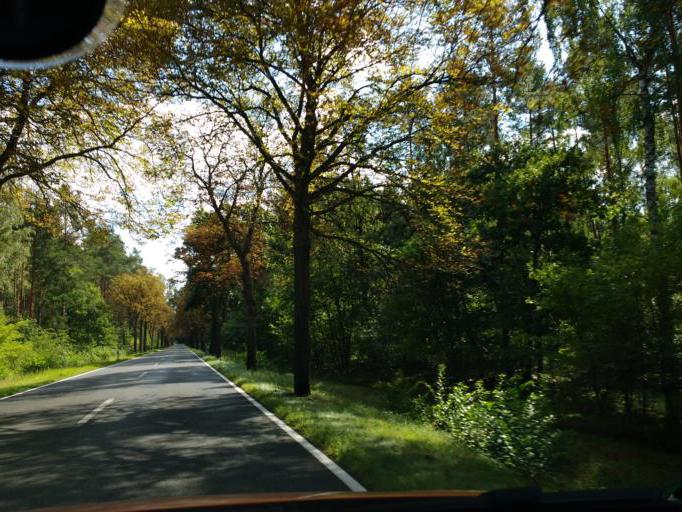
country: DE
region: Brandenburg
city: Oranienburg
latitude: 52.7382
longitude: 13.2804
